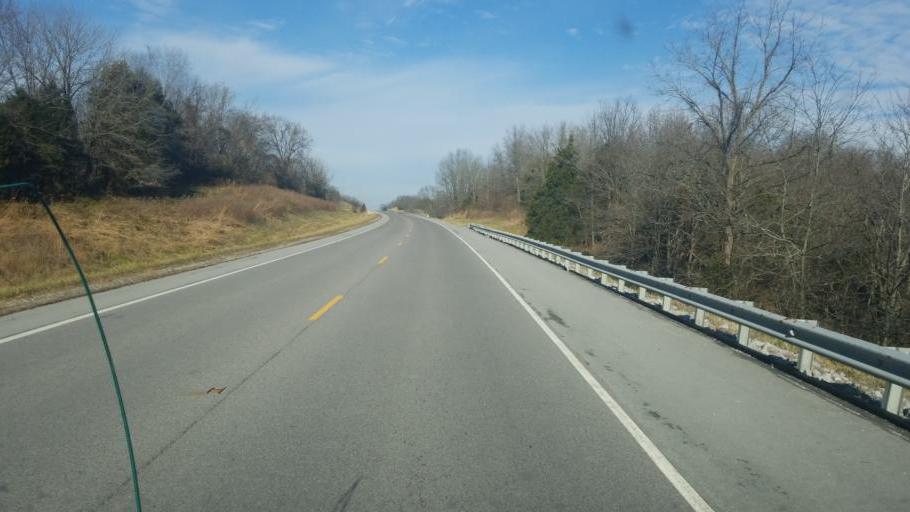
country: US
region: Illinois
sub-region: Union County
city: Cobden
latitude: 37.5423
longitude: -89.2217
